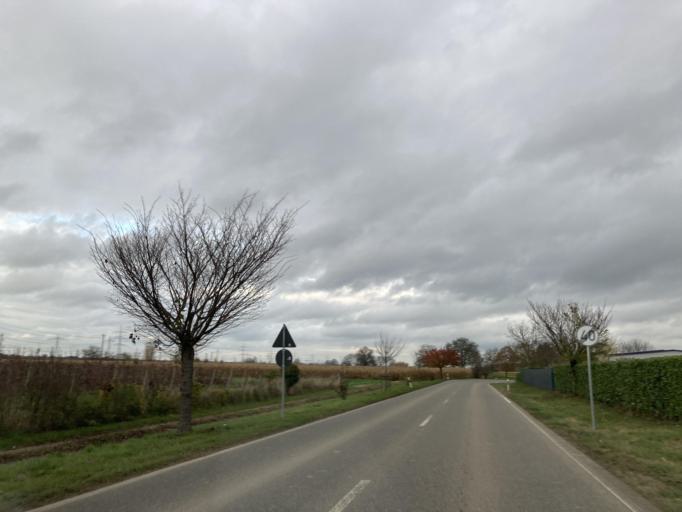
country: DE
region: Baden-Wuerttemberg
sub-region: Freiburg Region
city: Schliengen
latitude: 47.7632
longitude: 7.5731
